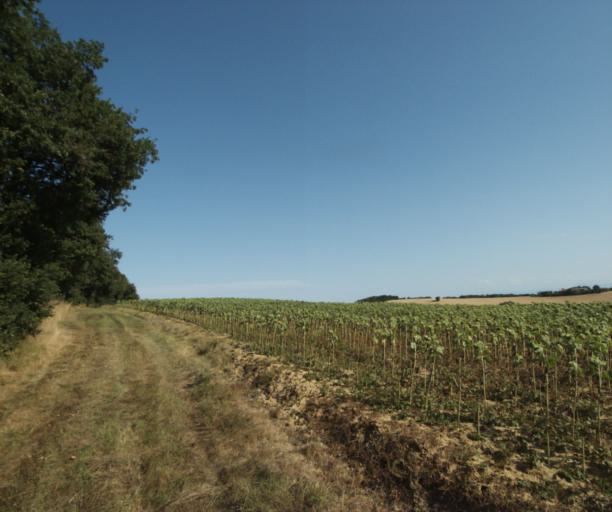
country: FR
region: Midi-Pyrenees
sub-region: Departement de la Haute-Garonne
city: Avignonet-Lauragais
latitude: 43.4262
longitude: 1.8025
